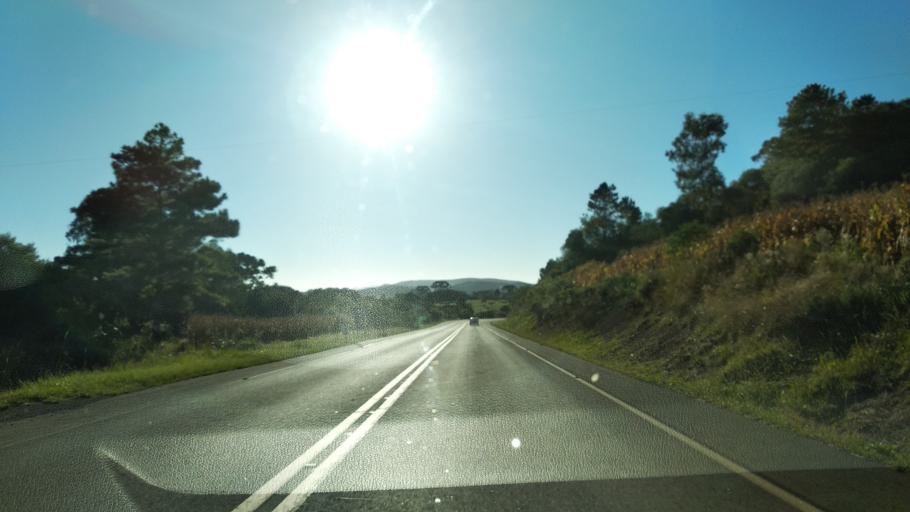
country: BR
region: Santa Catarina
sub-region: Lages
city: Lages
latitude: -27.7854
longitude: -50.4502
